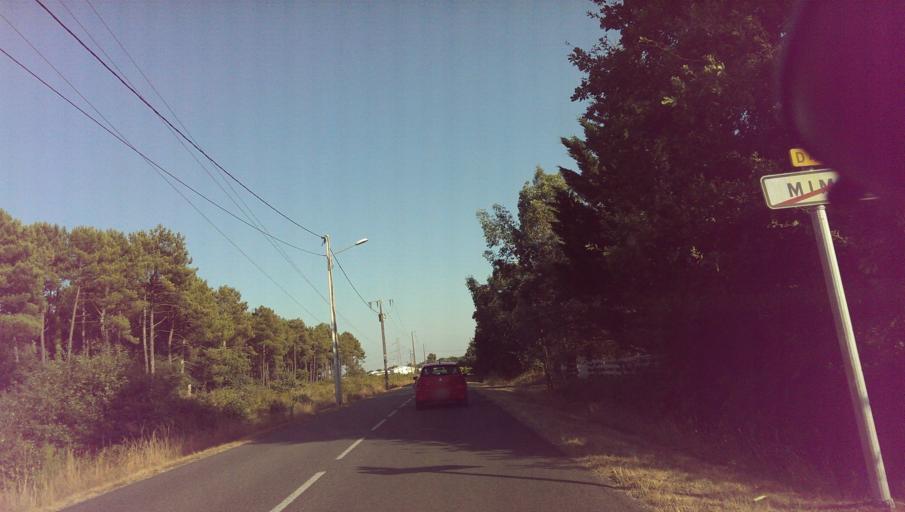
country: FR
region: Aquitaine
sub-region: Departement des Landes
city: Mimizan
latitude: 44.1936
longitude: -1.2197
